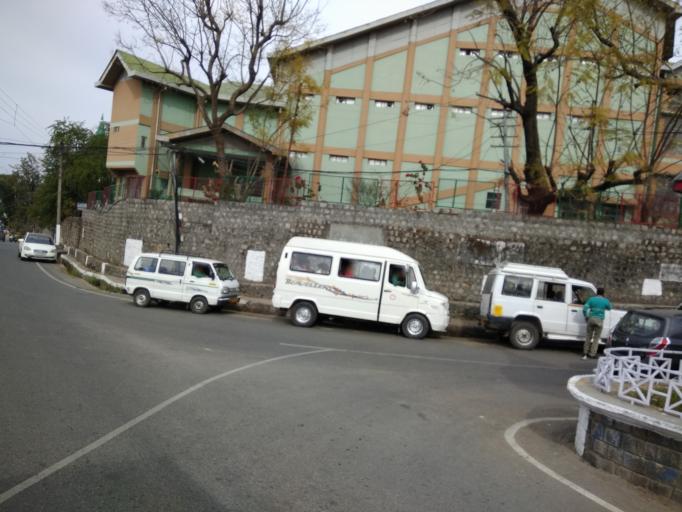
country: IN
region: Himachal Pradesh
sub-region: Kangra
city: Dharmsala
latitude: 32.1905
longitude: 76.3528
